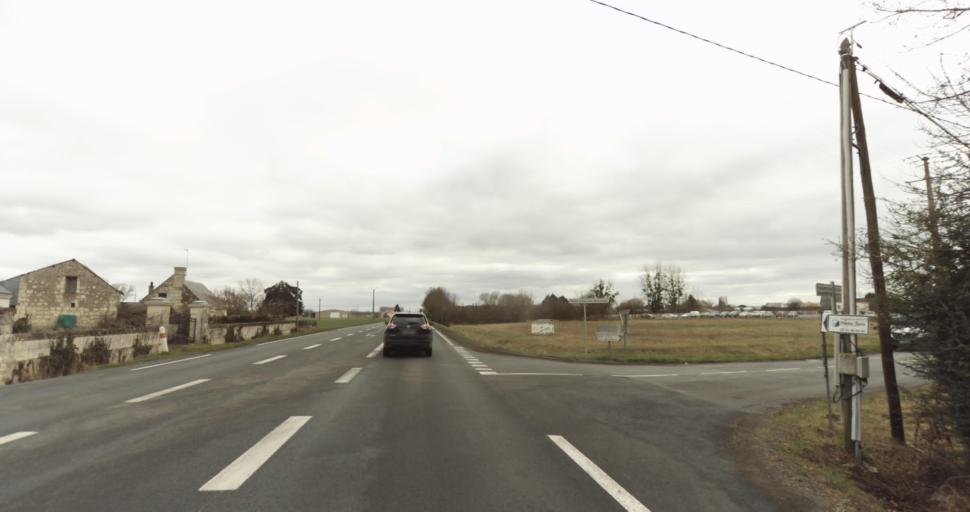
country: FR
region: Pays de la Loire
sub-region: Departement de Maine-et-Loire
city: Vivy
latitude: 47.3157
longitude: -0.0463
